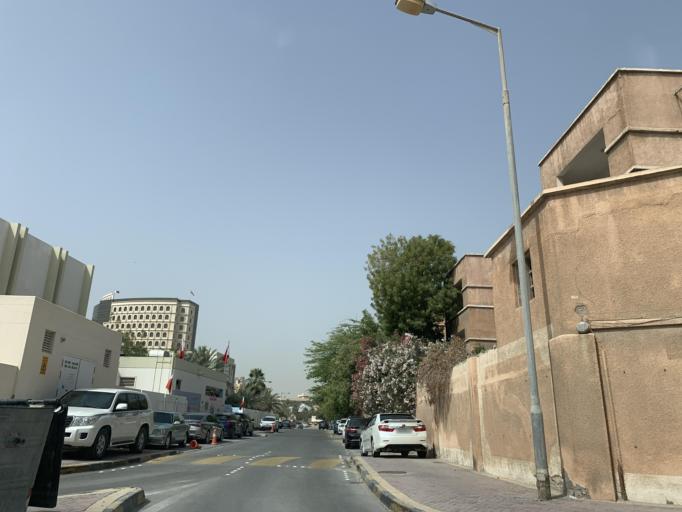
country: BH
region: Manama
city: Manama
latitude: 26.2081
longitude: 50.6005
